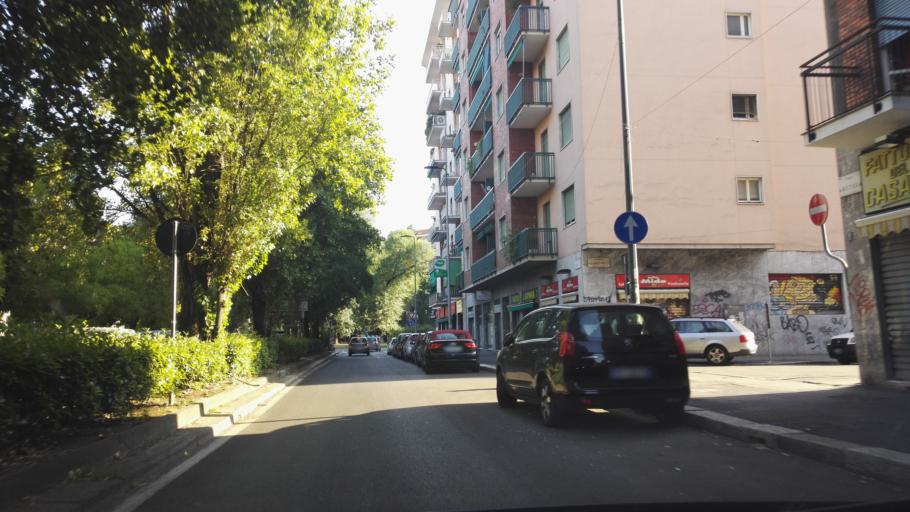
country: IT
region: Lombardy
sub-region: Citta metropolitana di Milano
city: Romano Banco
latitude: 45.4664
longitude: 9.1368
